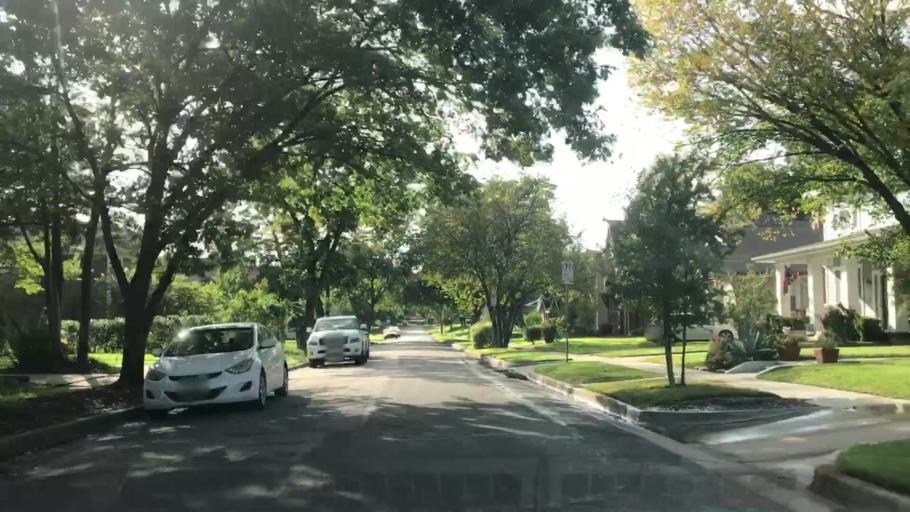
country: US
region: Texas
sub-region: Dallas County
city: Highland Park
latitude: 32.8213
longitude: -96.7728
